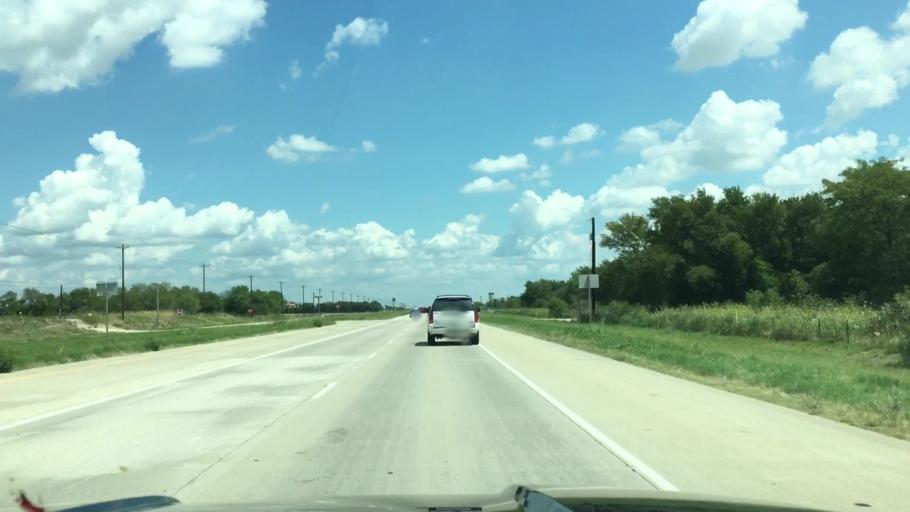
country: US
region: Texas
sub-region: Tarrant County
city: Haslet
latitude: 33.0354
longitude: -97.3638
